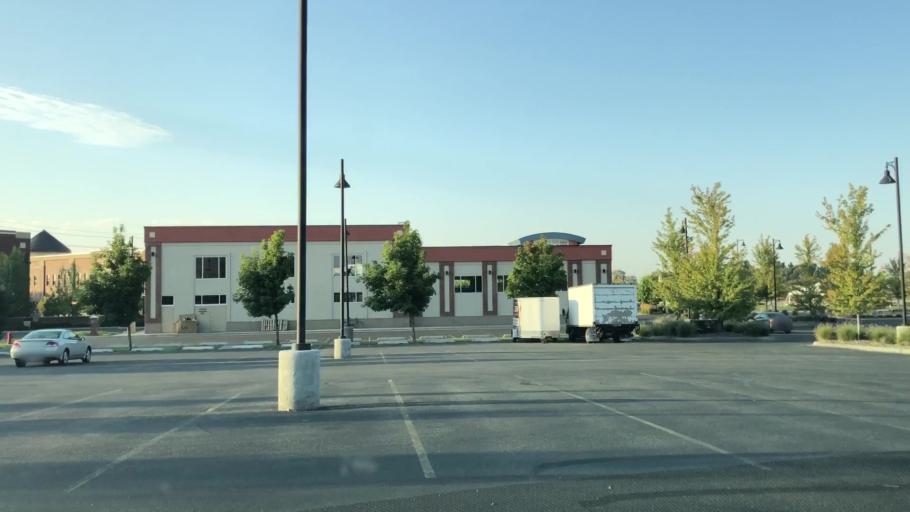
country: US
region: Idaho
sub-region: Bonneville County
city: Idaho Falls
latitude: 43.4849
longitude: -112.0519
